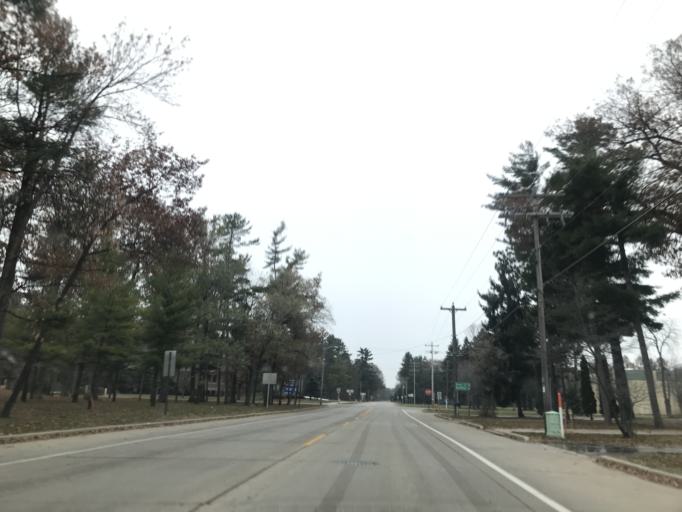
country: US
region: Wisconsin
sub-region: Marinette County
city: Marinette
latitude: 45.0717
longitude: -87.6194
